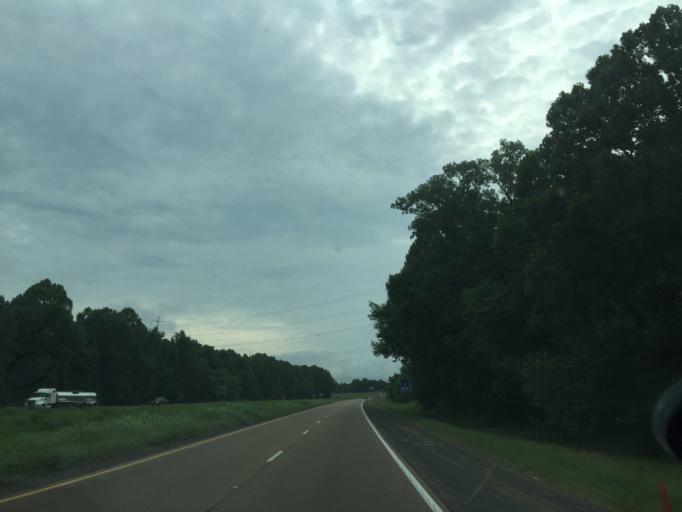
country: US
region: Mississippi
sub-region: Rankin County
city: Brandon
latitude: 32.2800
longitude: -90.0201
